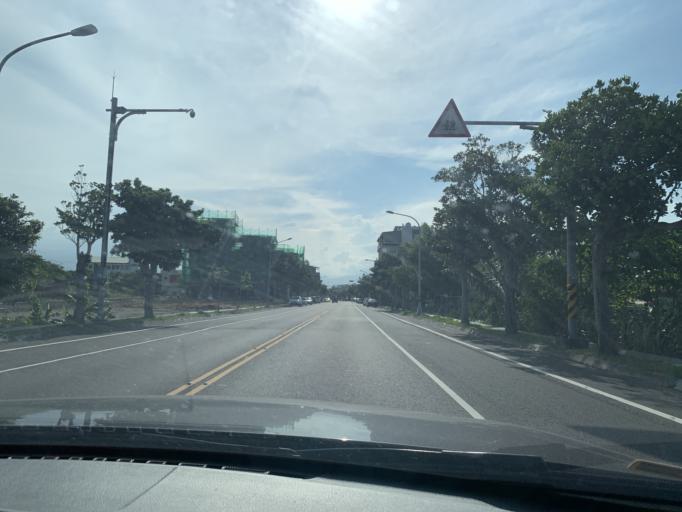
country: TW
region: Taiwan
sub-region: Yilan
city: Yilan
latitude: 24.6686
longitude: 121.8255
